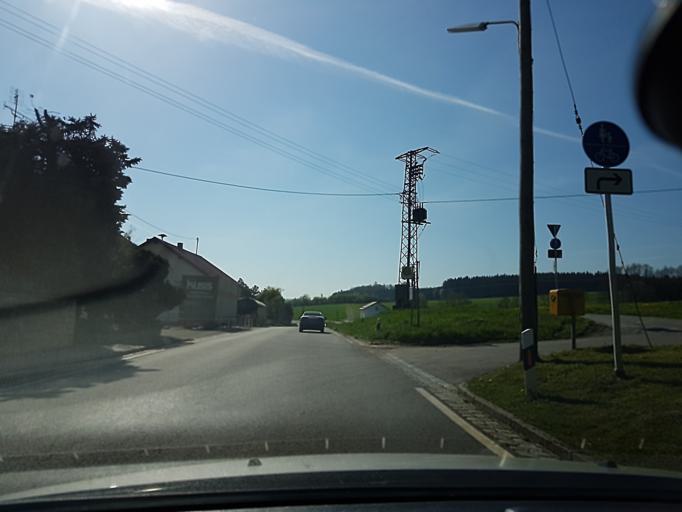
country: DE
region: Bavaria
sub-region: Upper Bavaria
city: Neumarkt-Sankt Veit
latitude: 48.3741
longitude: 12.4792
